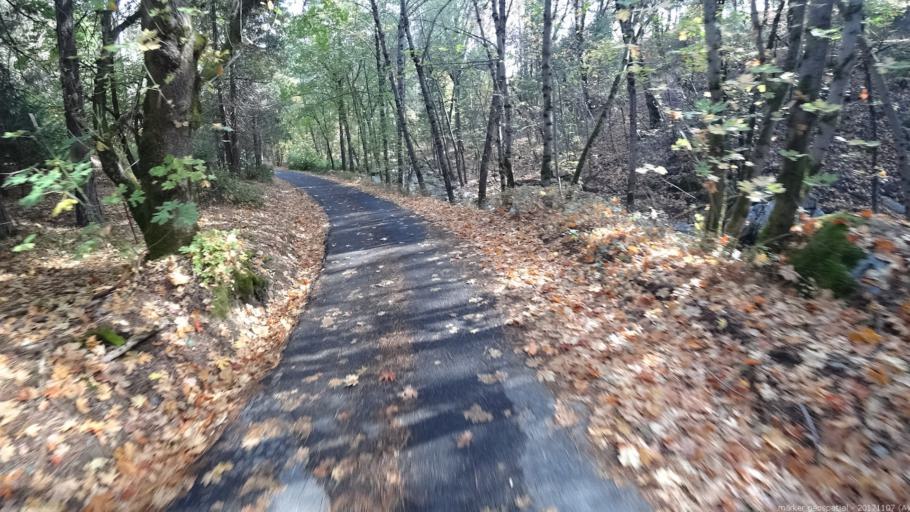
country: US
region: California
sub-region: Shasta County
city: Shasta
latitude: 40.5444
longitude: -122.5737
